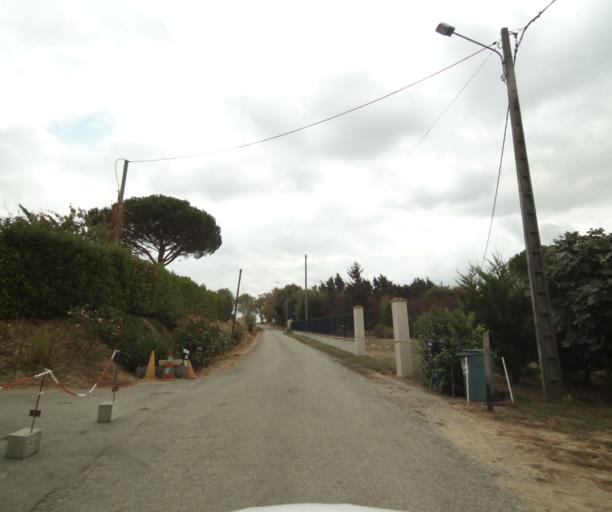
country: FR
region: Midi-Pyrenees
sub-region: Departement de la Haute-Garonne
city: Villefranche-de-Lauragais
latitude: 43.4149
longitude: 1.7139
